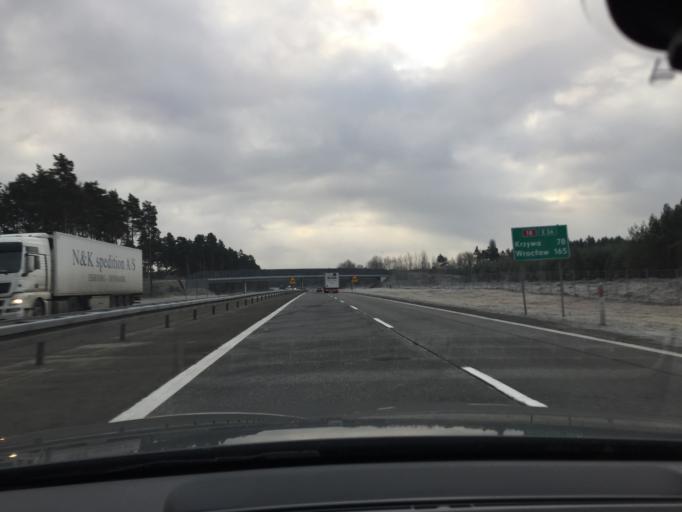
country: PL
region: Lubusz
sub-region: Powiat zarski
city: Trzebiel
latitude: 51.6326
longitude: 14.8759
